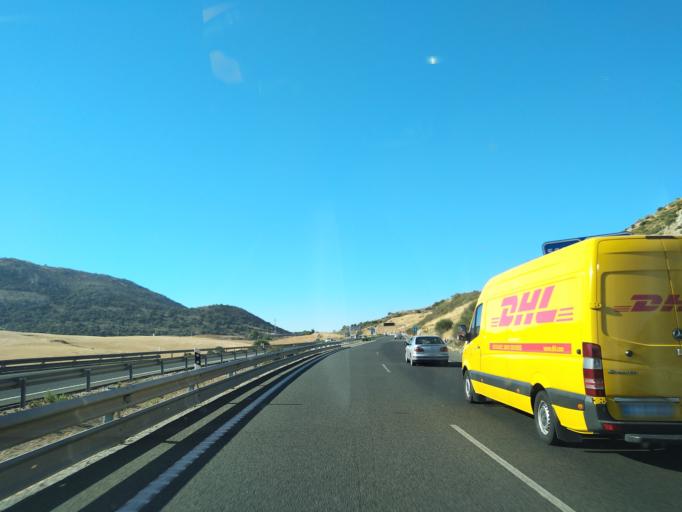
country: ES
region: Andalusia
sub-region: Provincia de Malaga
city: Villanueva del Rosario
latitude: 36.9765
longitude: -4.4446
